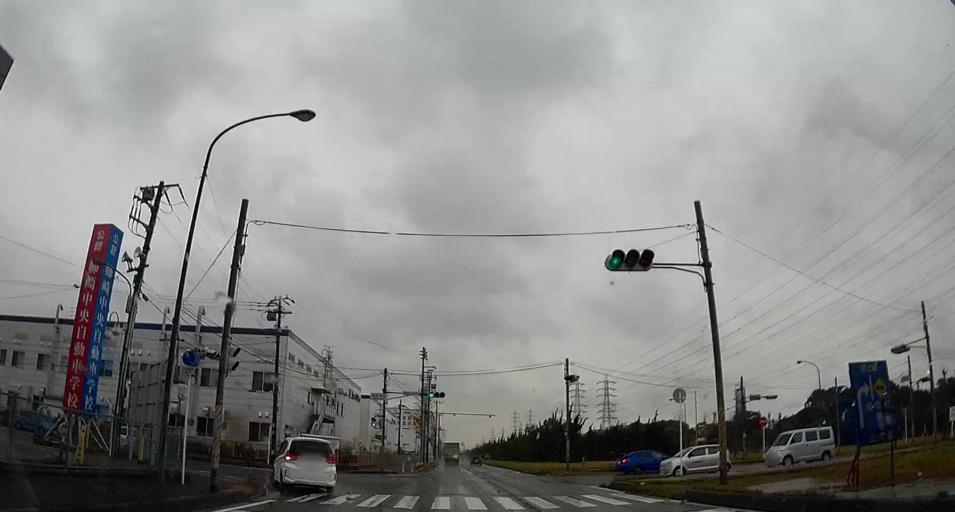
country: JP
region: Chiba
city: Ichihara
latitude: 35.4844
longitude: 140.0387
